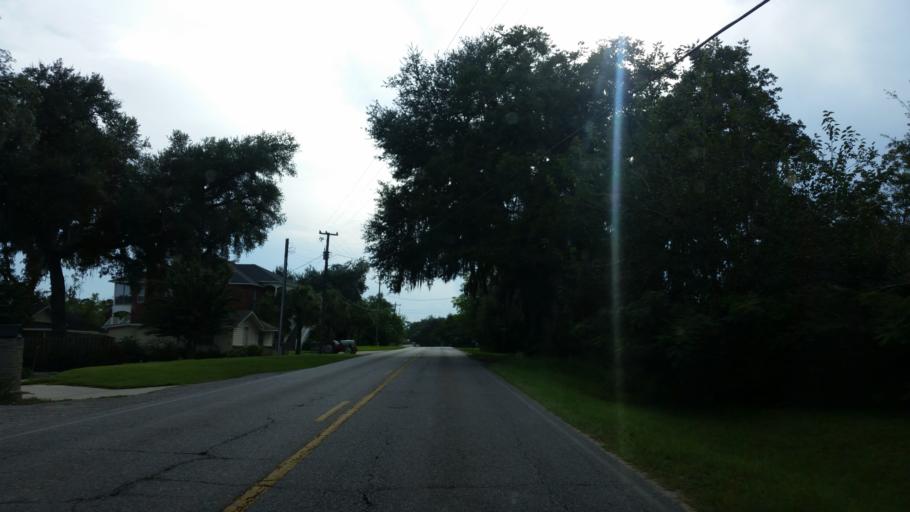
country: US
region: Florida
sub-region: Santa Rosa County
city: Milton
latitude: 30.6350
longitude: -87.0341
